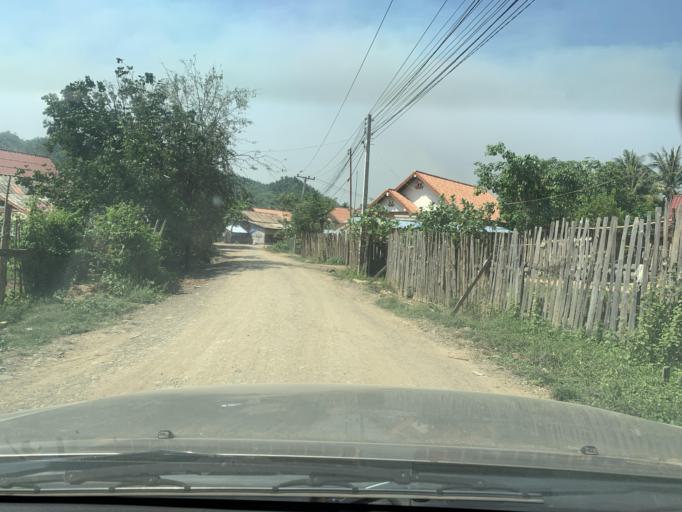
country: LA
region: Louangphabang
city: Louangphabang
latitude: 19.9312
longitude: 102.2772
